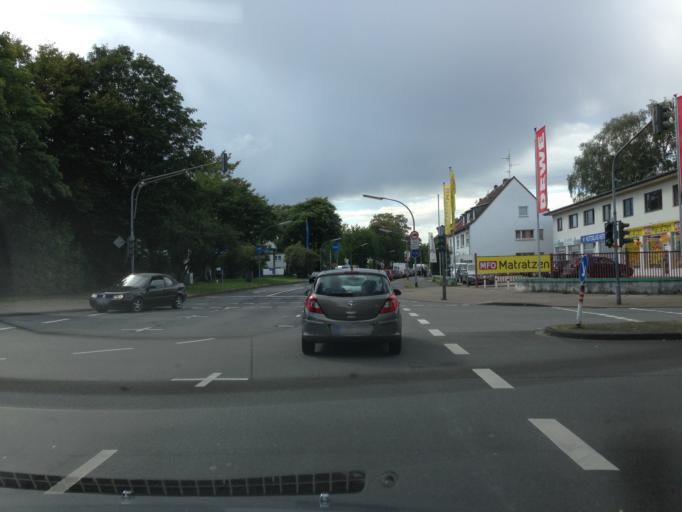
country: DE
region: North Rhine-Westphalia
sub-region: Regierungsbezirk Koln
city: Eil
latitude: 50.8917
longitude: 7.0695
